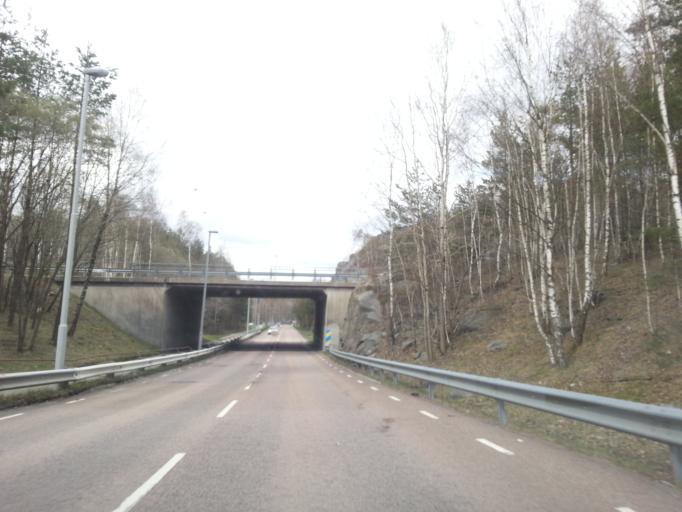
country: SE
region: Vaestra Goetaland
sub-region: Goteborg
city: Hammarkullen
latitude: 57.7872
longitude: 12.0359
